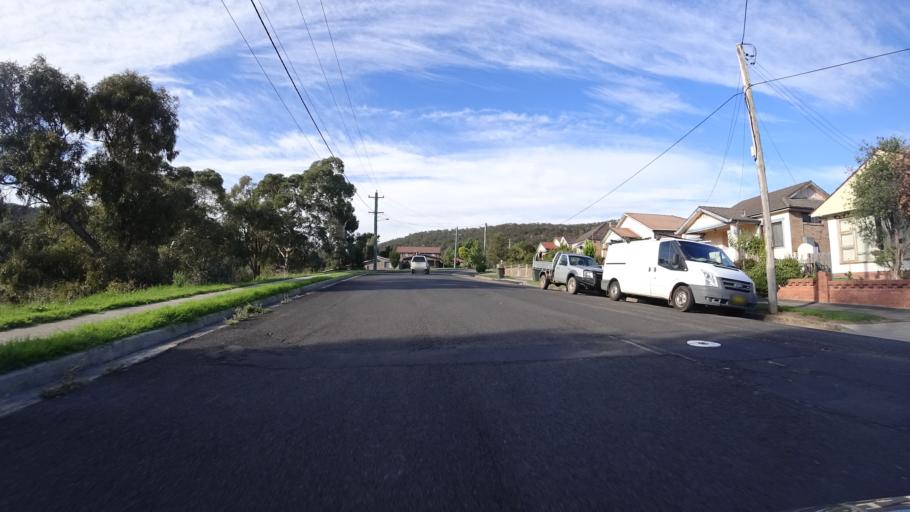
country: AU
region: New South Wales
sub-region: Lithgow
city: Lithgow
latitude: -33.4884
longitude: 150.1515
